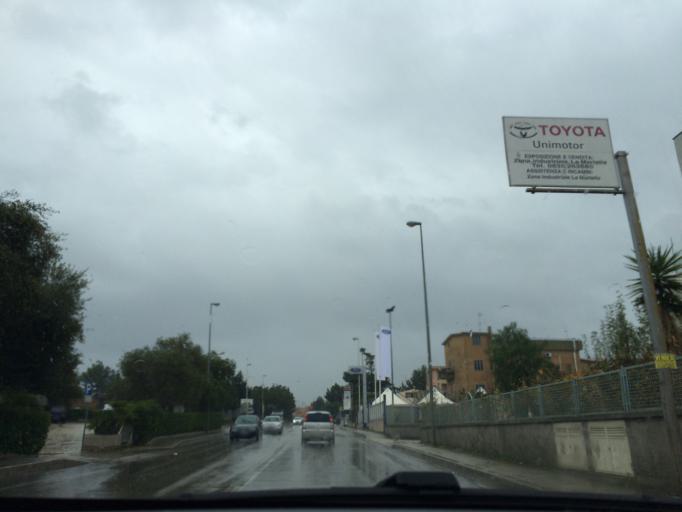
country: IT
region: Basilicate
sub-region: Provincia di Matera
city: Matera
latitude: 40.6809
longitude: 16.5833
